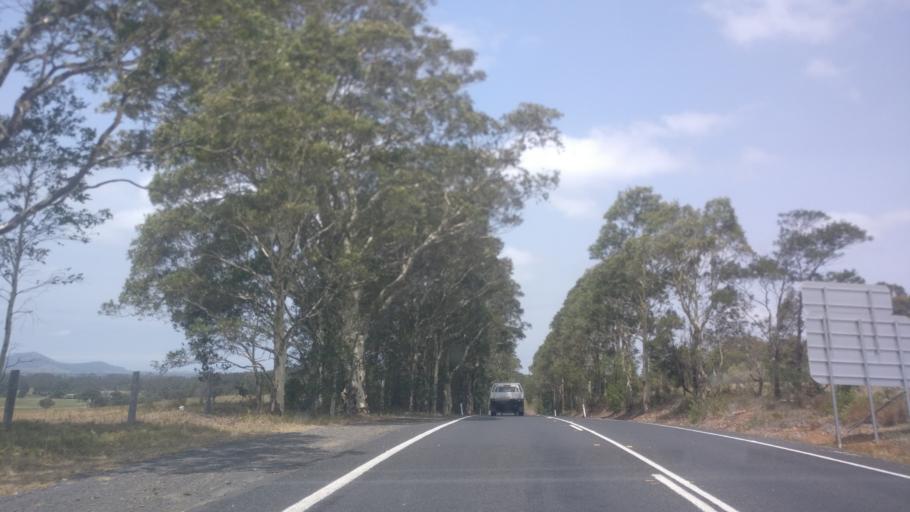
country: AU
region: New South Wales
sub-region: Shoalhaven Shire
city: Bomaderry
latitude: -34.8256
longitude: 150.5724
